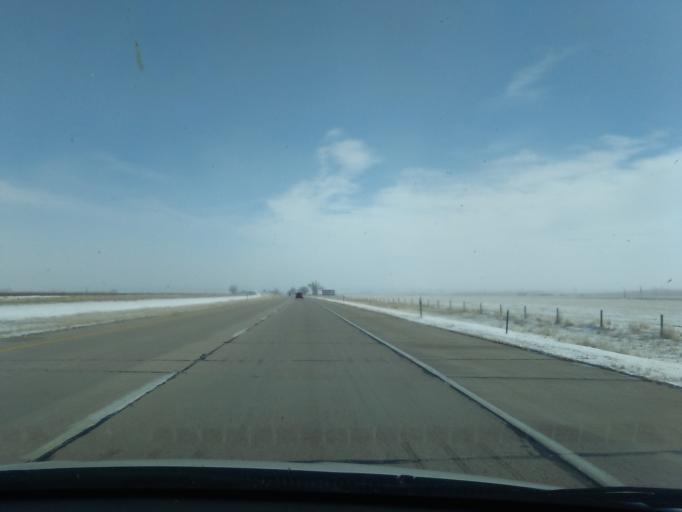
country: US
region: Wyoming
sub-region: Laramie County
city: Pine Bluffs
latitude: 41.1477
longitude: -104.1735
